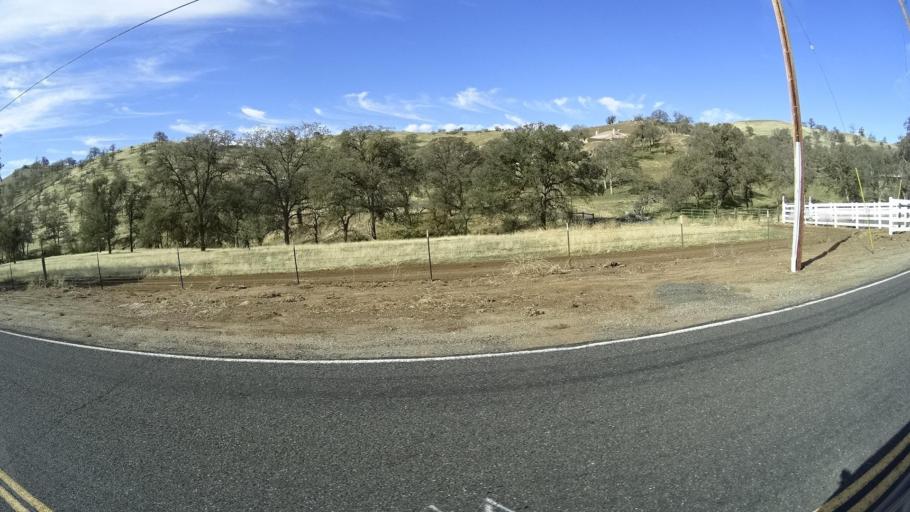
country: US
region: California
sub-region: Kern County
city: Alta Sierra
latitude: 35.6358
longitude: -118.8013
